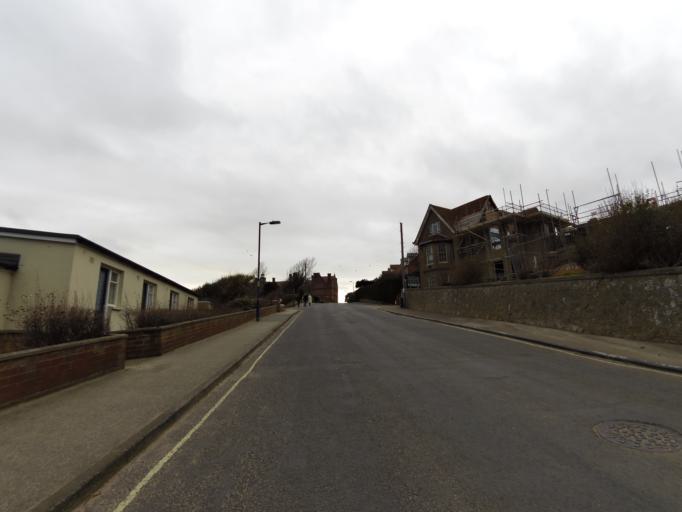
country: GB
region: England
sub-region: Suffolk
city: Felixstowe
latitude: 51.9623
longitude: 1.3606
